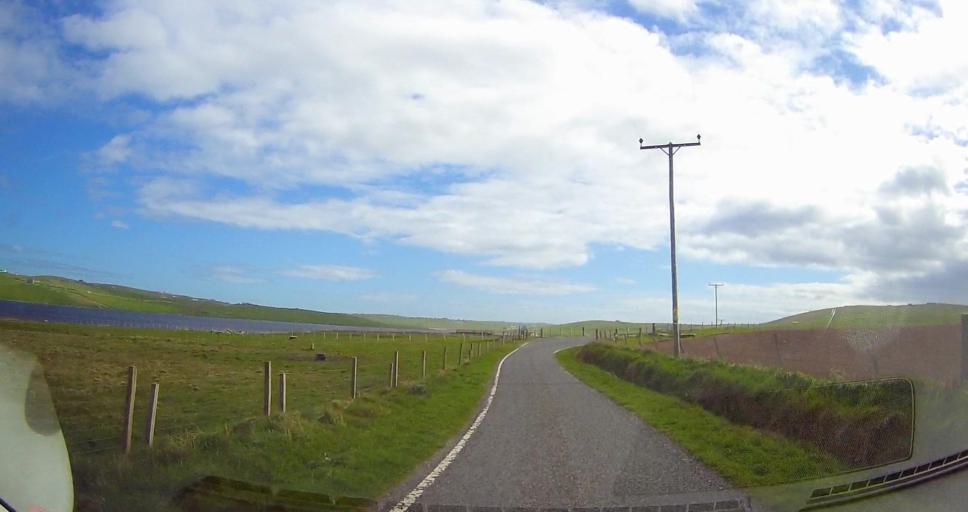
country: GB
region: Scotland
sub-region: Shetland Islands
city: Sandwick
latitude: 59.9399
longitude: -1.3462
